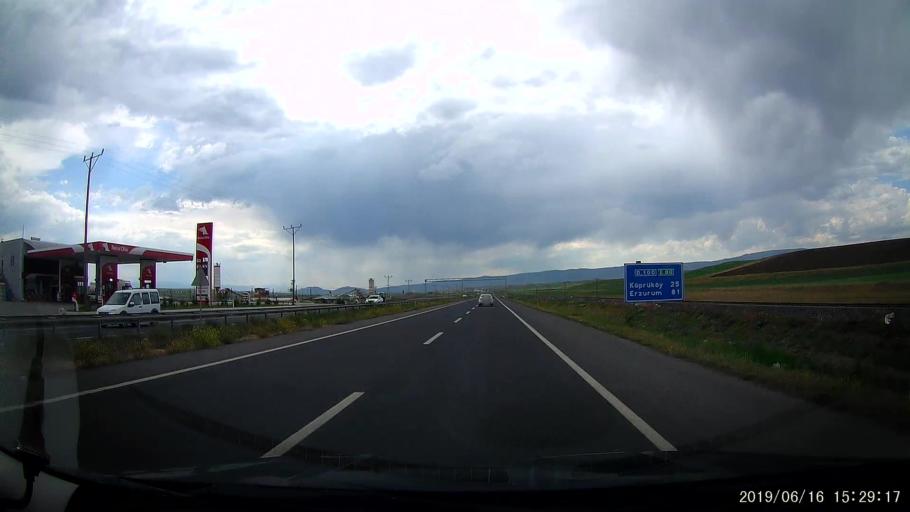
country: TR
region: Erzurum
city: Horasan
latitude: 40.0320
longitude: 42.1354
